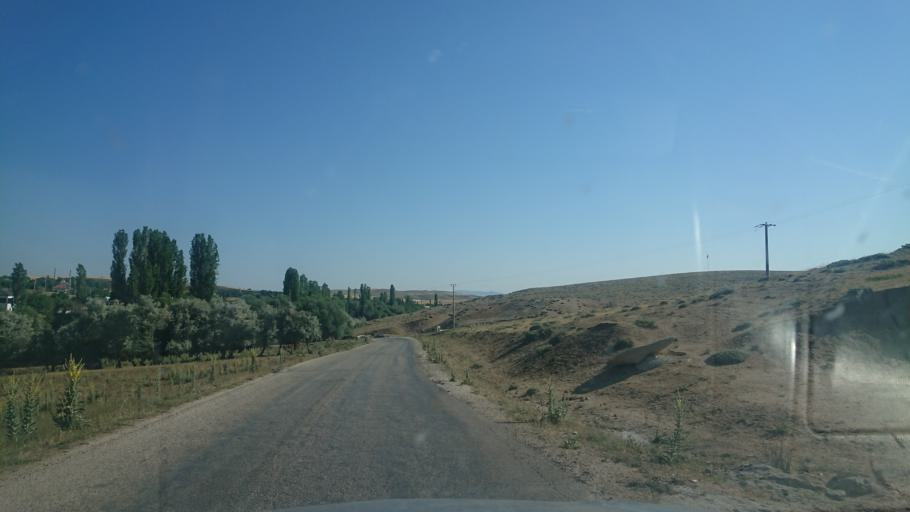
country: TR
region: Aksaray
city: Agacoren
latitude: 38.8783
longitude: 33.8808
